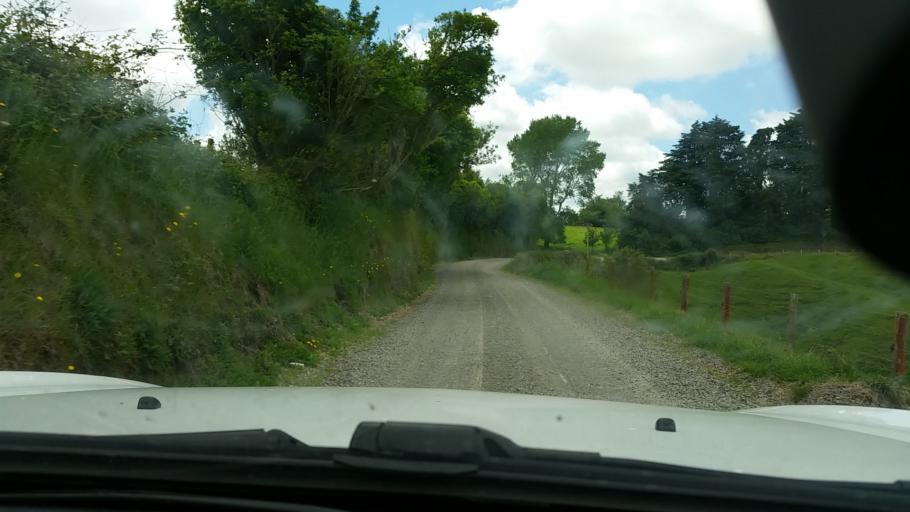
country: NZ
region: Bay of Plenty
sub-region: Western Bay of Plenty District
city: Maketu
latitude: -37.9628
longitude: 176.4354
